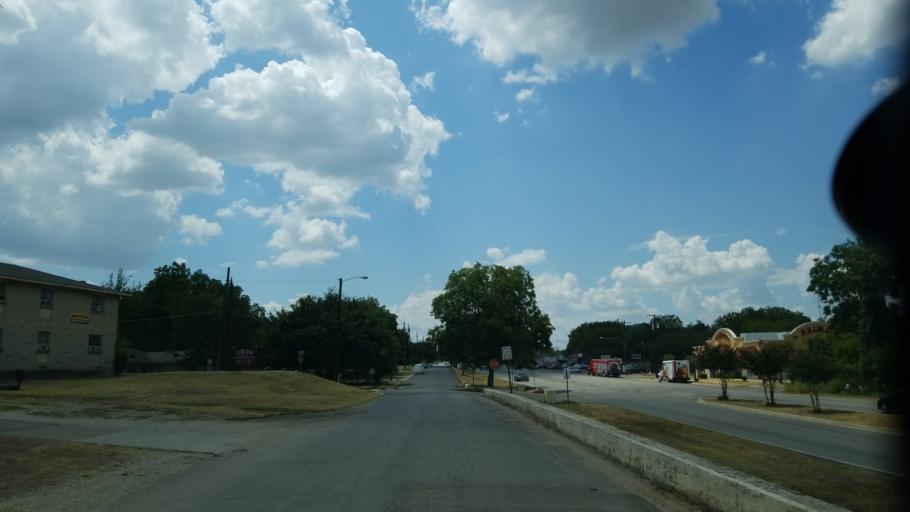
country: US
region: Texas
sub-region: Dallas County
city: Cockrell Hill
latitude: 32.7391
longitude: -96.8834
